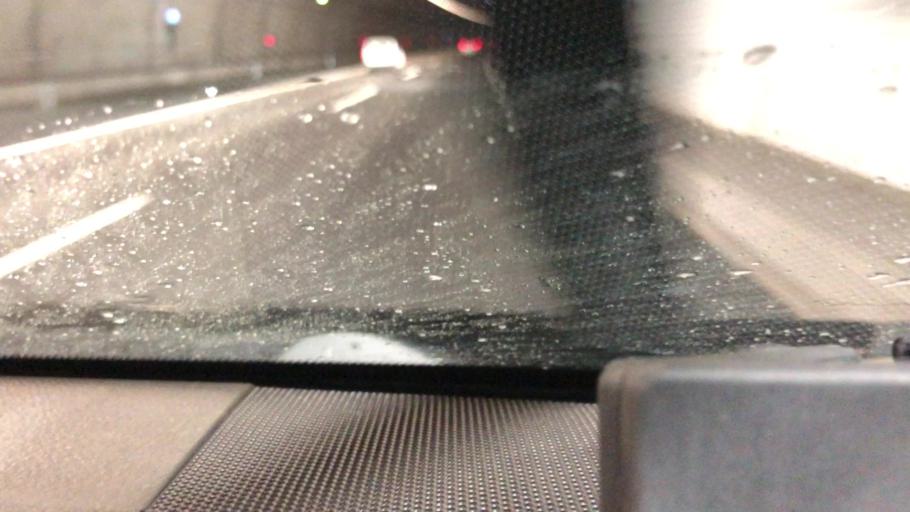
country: JP
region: Shizuoka
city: Gotemba
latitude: 35.2244
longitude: 138.8899
